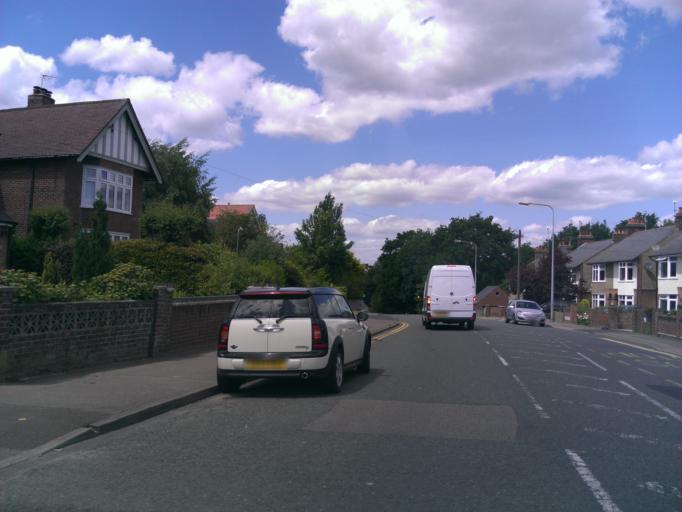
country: GB
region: England
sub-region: Essex
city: Colchester
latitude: 51.8757
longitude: 0.9227
